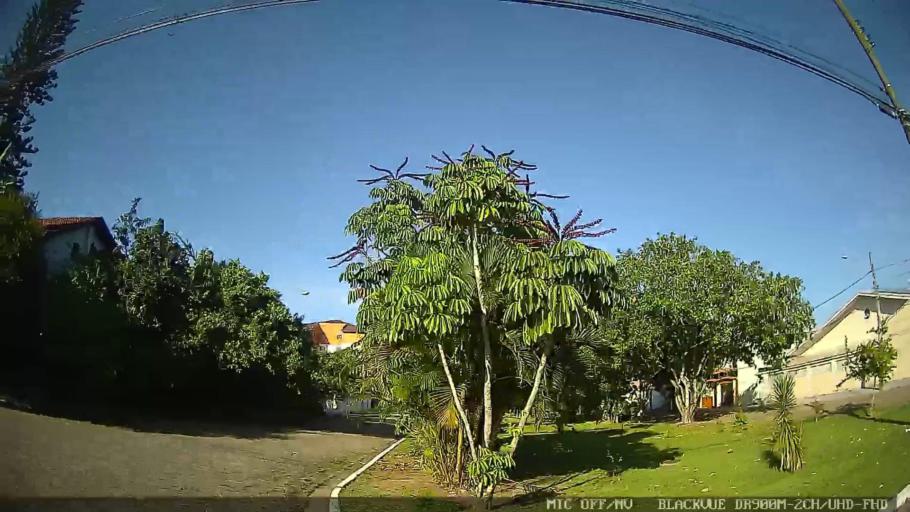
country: BR
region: Sao Paulo
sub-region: Peruibe
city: Peruibe
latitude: -24.3033
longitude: -46.9780
